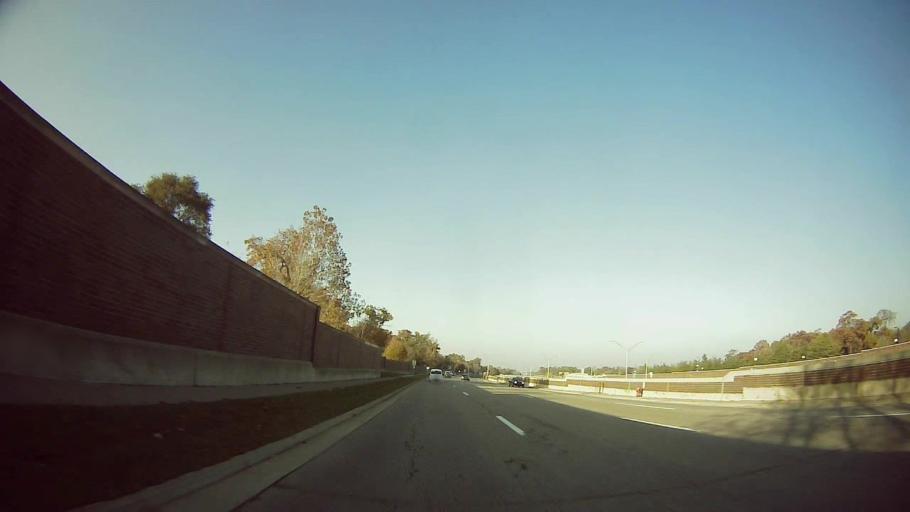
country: US
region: Michigan
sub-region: Oakland County
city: Pleasant Ridge
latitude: 42.4746
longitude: -83.1493
